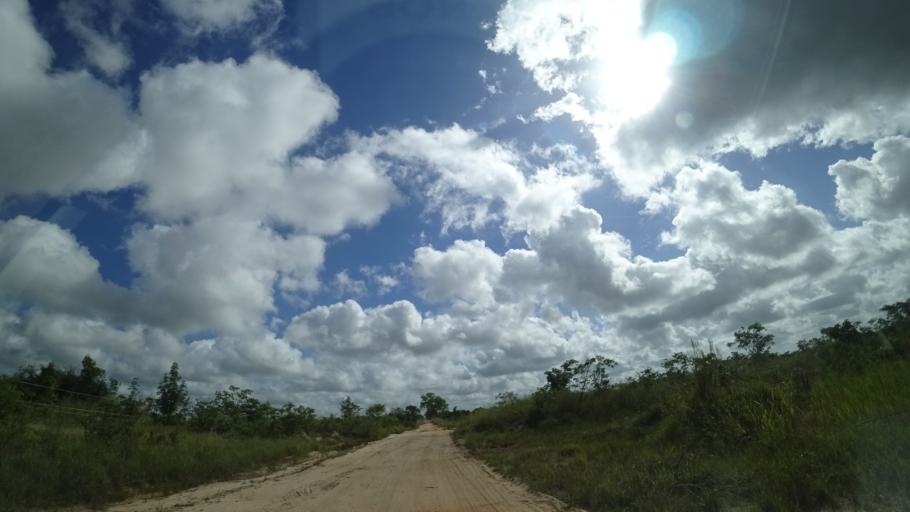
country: MZ
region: Sofala
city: Dondo
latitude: -19.4057
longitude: 34.7094
